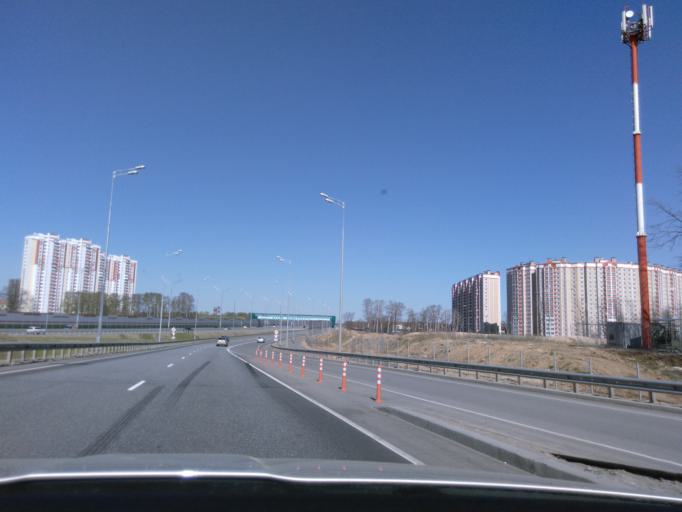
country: RU
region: Moskovskaya
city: Levoberezhnaya
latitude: 55.9017
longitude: 37.4867
